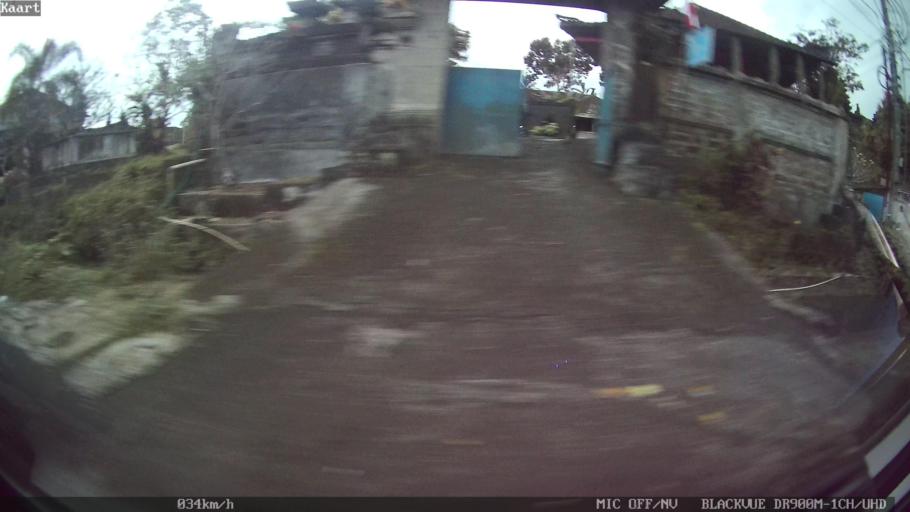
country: ID
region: Bali
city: Empalan
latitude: -8.3803
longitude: 115.1514
